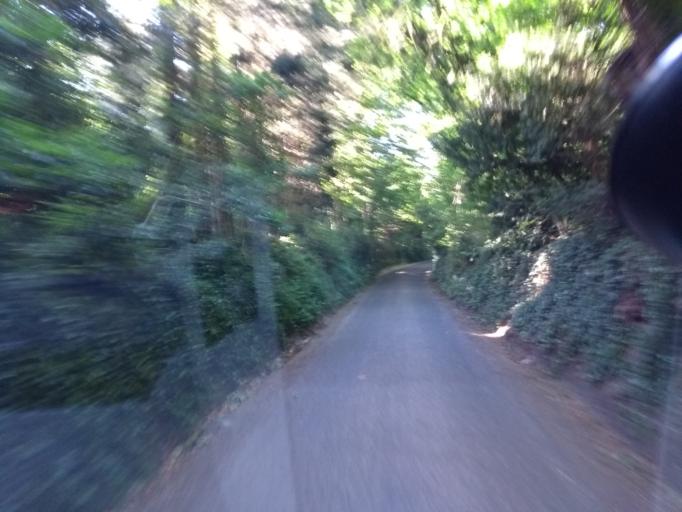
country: GB
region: England
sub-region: Somerset
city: Creech Saint Michael
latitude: 51.0483
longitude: -3.0532
